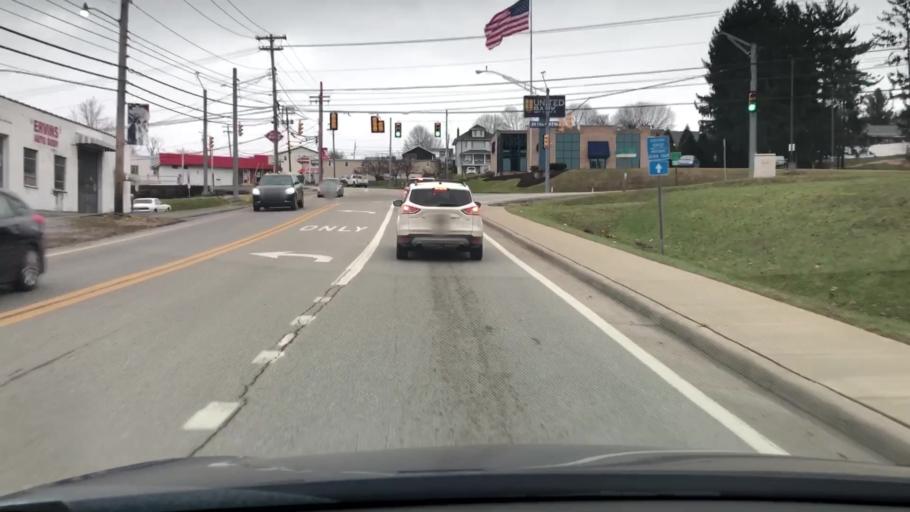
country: US
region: West Virginia
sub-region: Monongalia County
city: Westover
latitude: 39.6324
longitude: -79.9762
